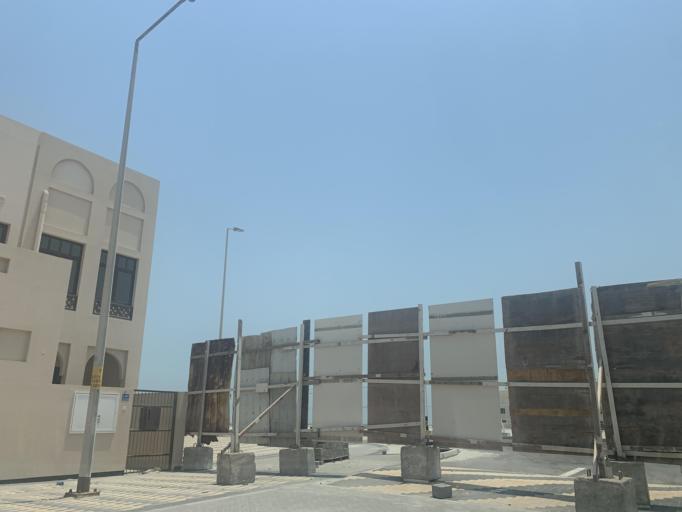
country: BH
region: Muharraq
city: Al Hadd
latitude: 26.2401
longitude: 50.6722
